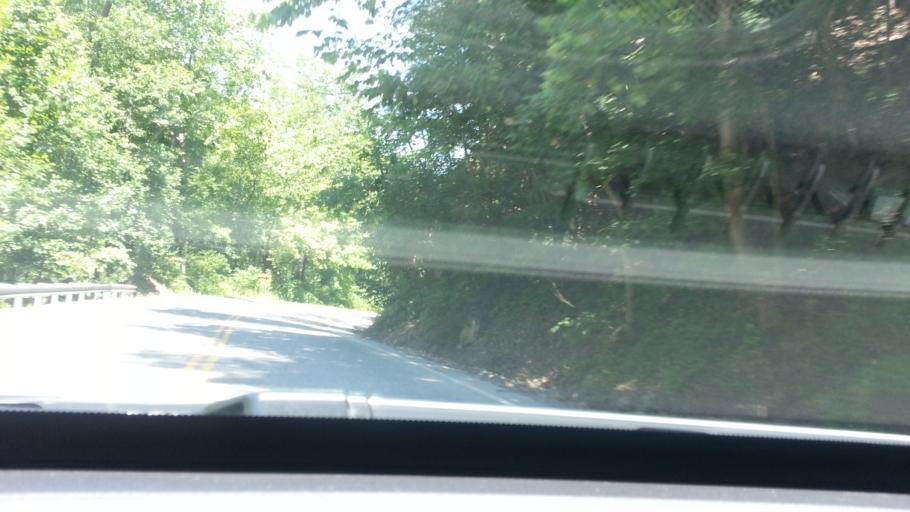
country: US
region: West Virginia
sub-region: Fayette County
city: Ansted
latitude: 38.1109
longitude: -81.1465
